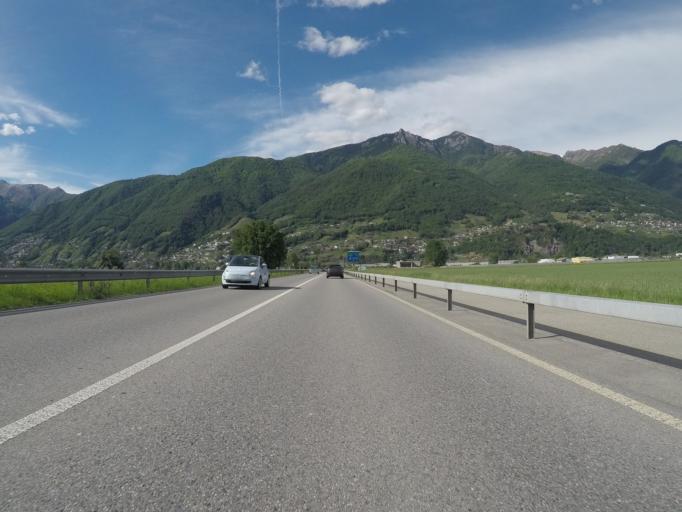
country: CH
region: Ticino
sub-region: Locarno District
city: Gordola
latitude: 46.1654
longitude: 8.8859
